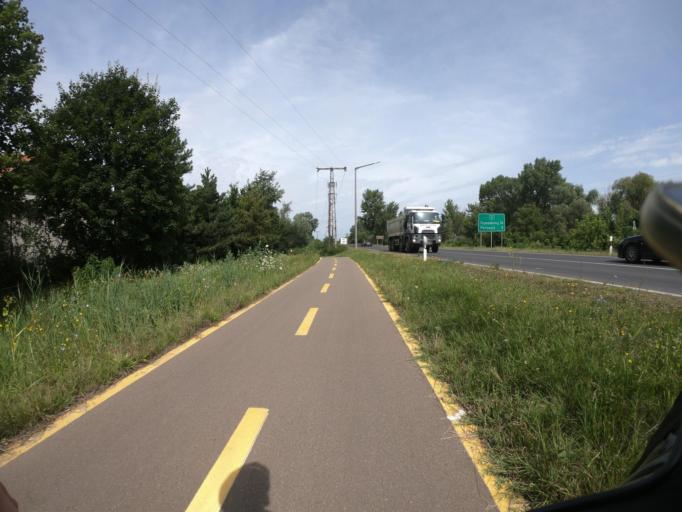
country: HU
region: Jasz-Nagykun-Szolnok
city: Tiszafured
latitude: 47.6290
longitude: 20.7470
